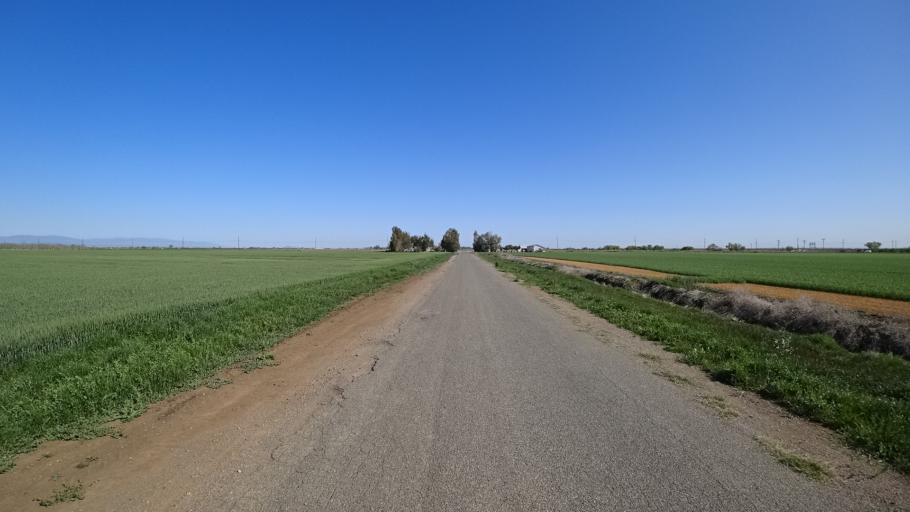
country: US
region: California
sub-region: Glenn County
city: Willows
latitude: 39.5504
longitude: -122.1983
